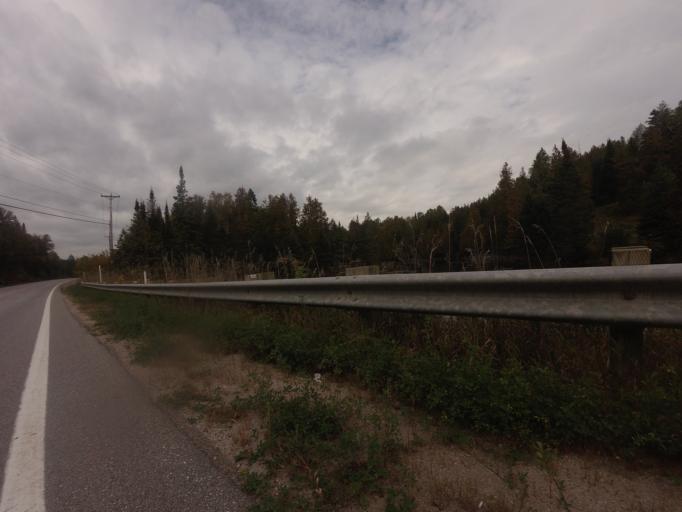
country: CA
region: Quebec
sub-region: Outaouais
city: Wakefield
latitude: 45.9329
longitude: -75.9901
